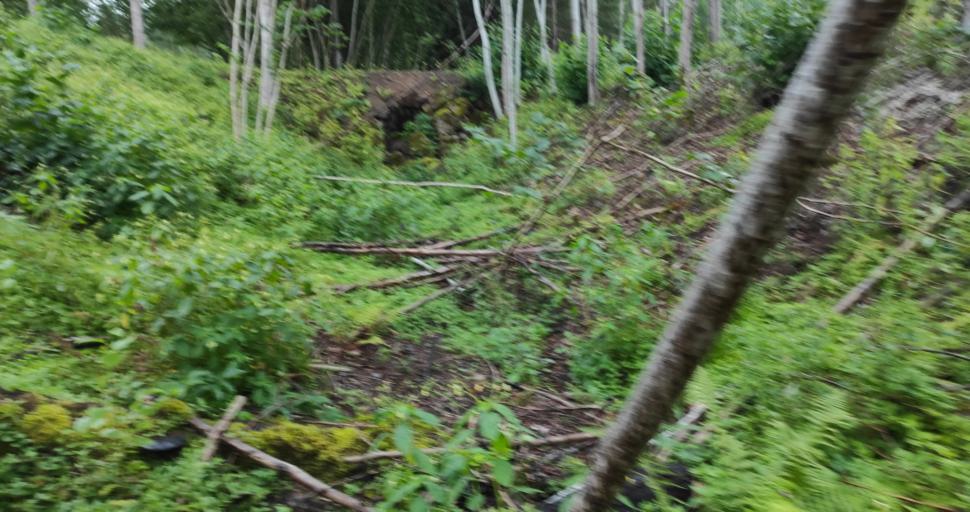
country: LV
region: Talsu Rajons
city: Talsi
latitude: 57.2047
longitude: 22.7240
